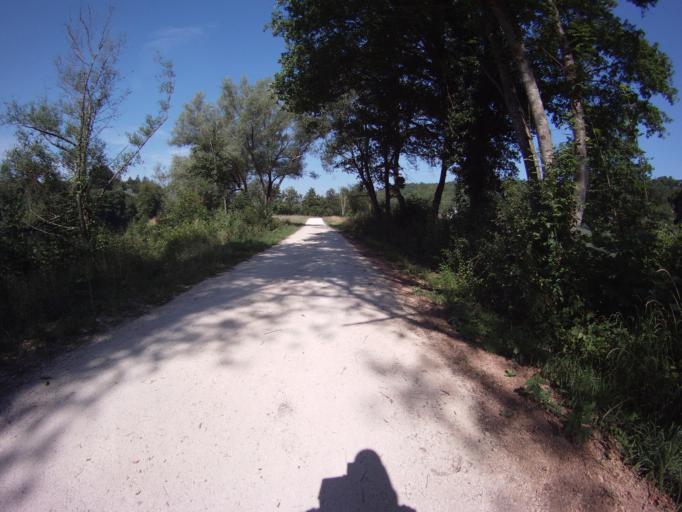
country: FR
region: Lorraine
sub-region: Departement de Meurthe-et-Moselle
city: Liverdun
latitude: 48.7571
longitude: 6.0603
